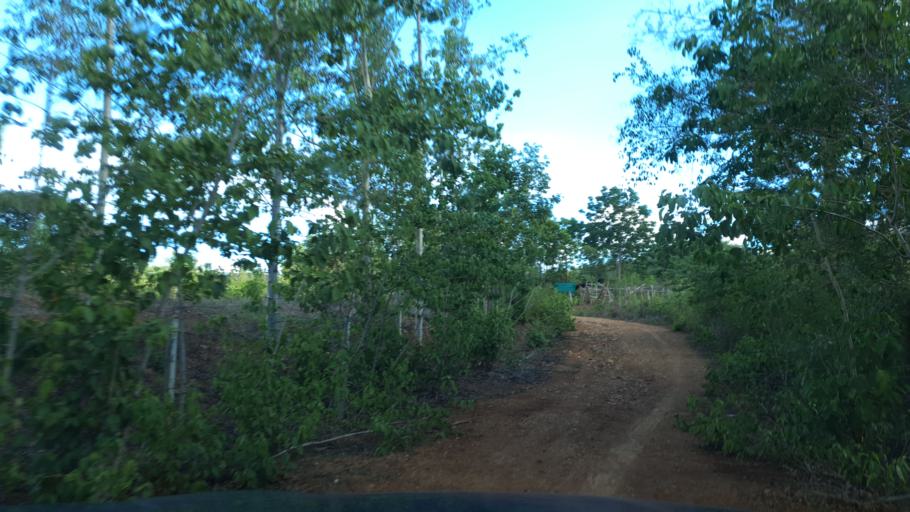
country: TH
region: Lampang
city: Sop Prap
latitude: 17.8538
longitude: 99.2835
